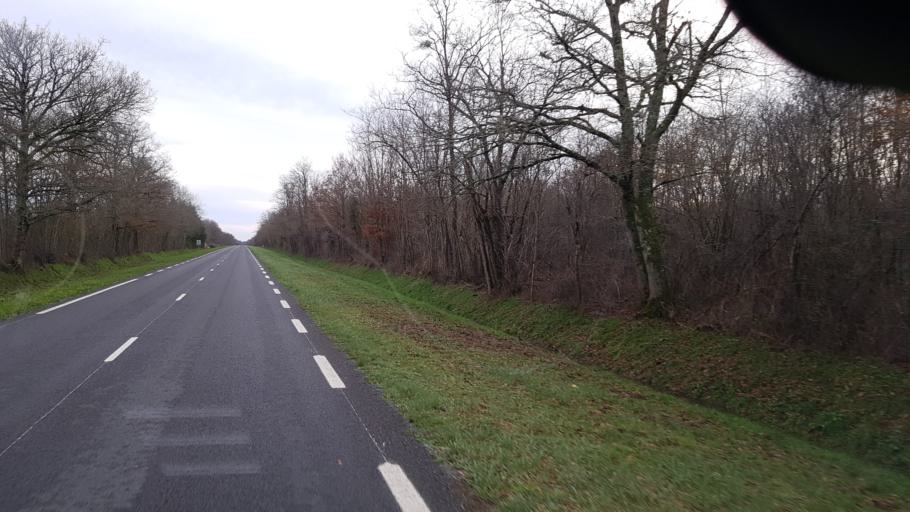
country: FR
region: Centre
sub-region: Departement du Loir-et-Cher
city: Salbris
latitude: 47.4795
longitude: 2.0399
